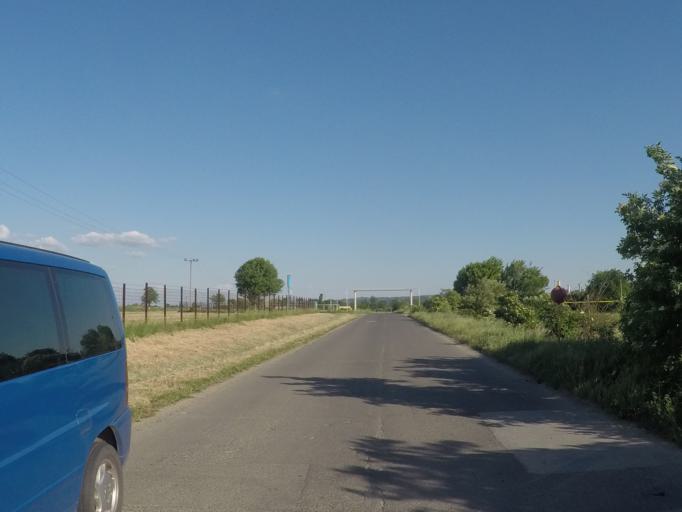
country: HU
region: Borsod-Abauj-Zemplen
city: Kazincbarcika
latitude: 48.2512
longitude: 20.6596
